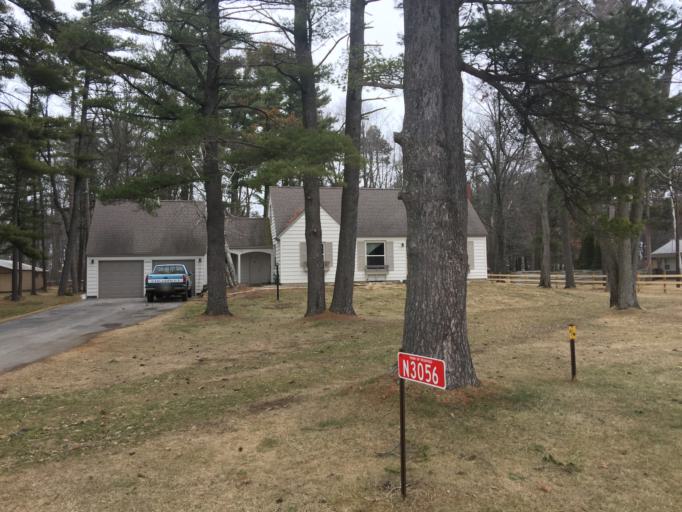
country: US
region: Wisconsin
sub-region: Marinette County
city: Marinette
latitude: 45.0693
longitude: -87.6193
